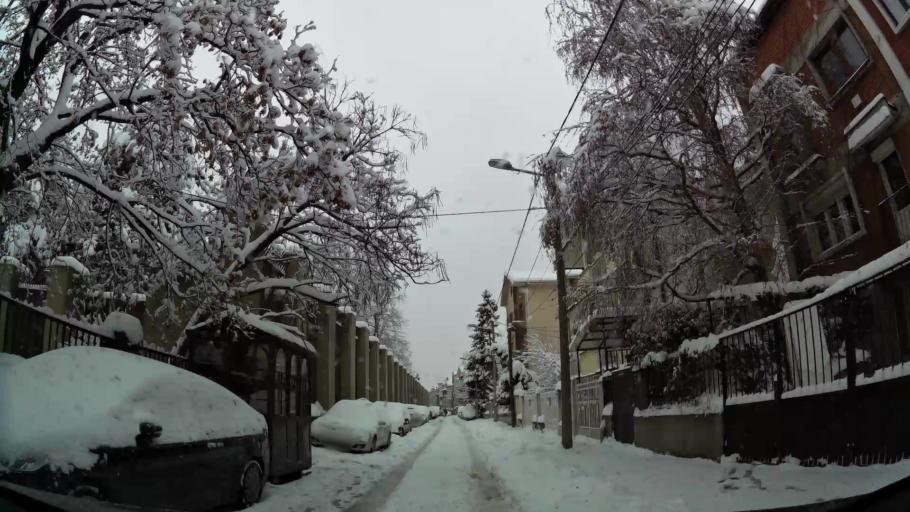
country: RS
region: Central Serbia
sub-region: Belgrade
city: Vracar
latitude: 44.7889
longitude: 20.4757
